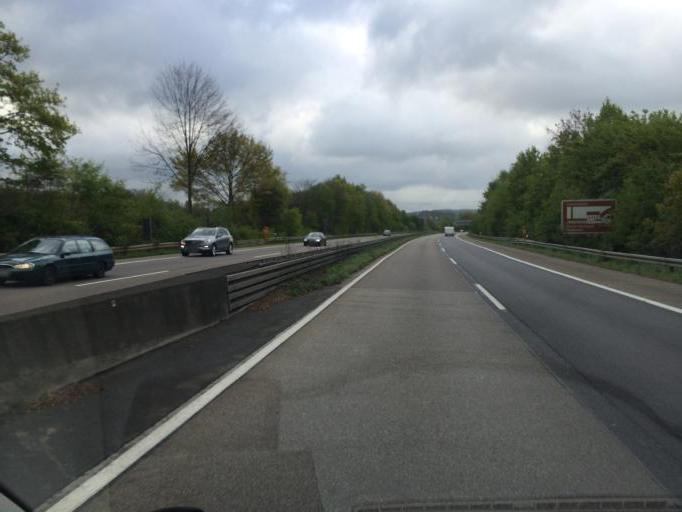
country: DE
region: North Rhine-Westphalia
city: Witten
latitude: 51.4498
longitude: 7.2922
